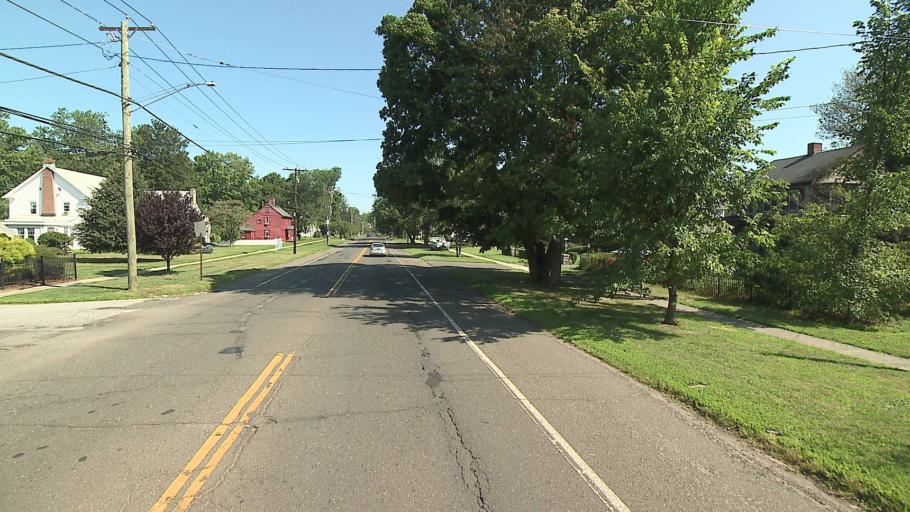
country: US
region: Connecticut
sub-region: Fairfield County
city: Stratford
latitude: 41.1806
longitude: -73.1303
